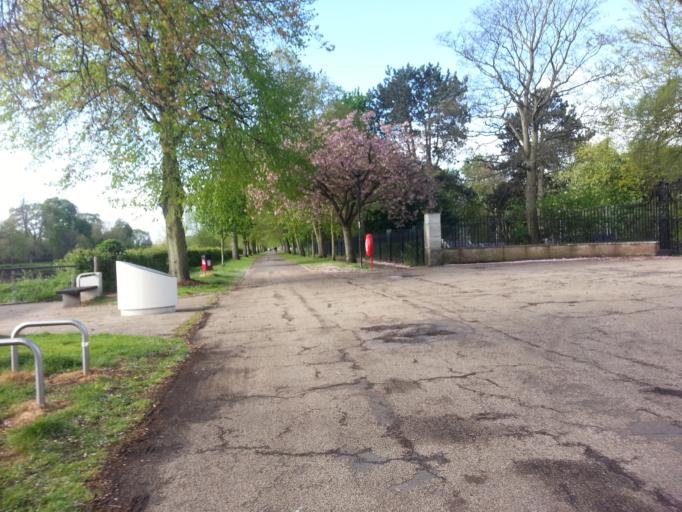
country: GB
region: England
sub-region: City of York
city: York
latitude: 53.9484
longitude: -1.0800
